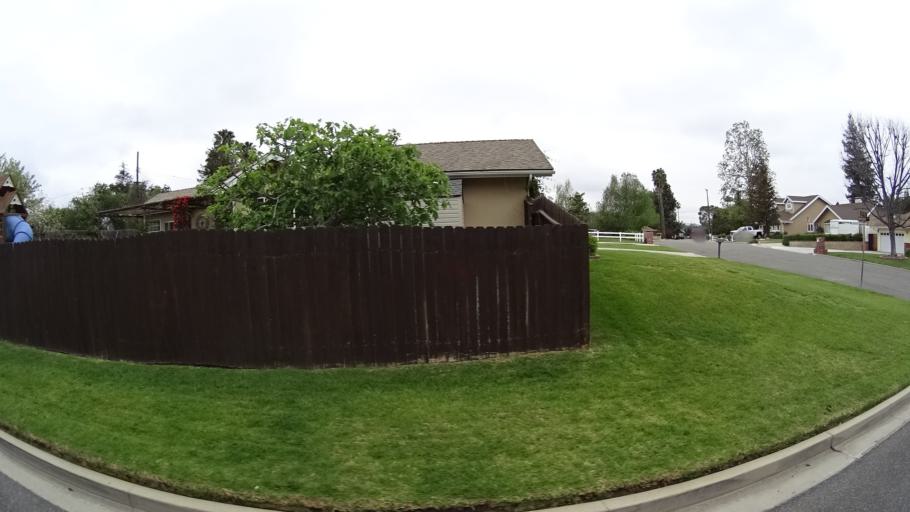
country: US
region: California
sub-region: Ventura County
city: Thousand Oaks
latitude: 34.2044
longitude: -118.8646
